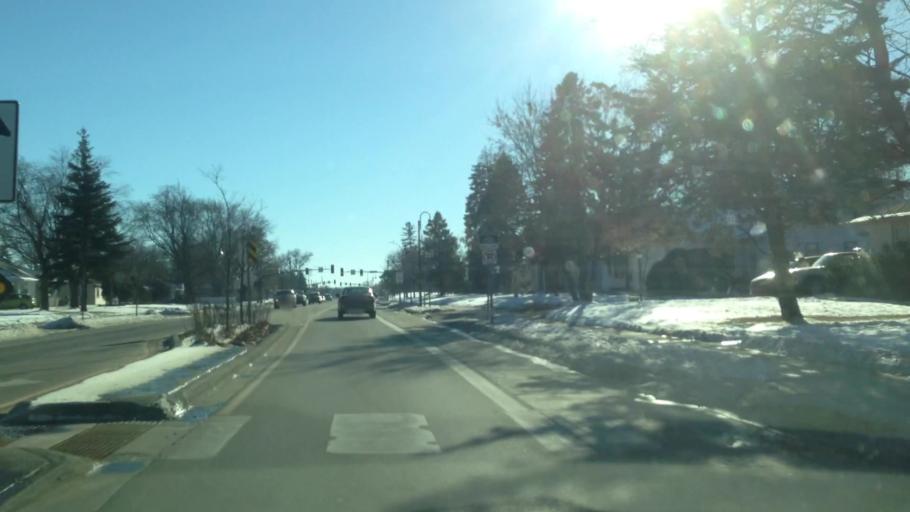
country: US
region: Minnesota
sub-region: Hennepin County
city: Richfield
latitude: 44.8673
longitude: -93.2682
